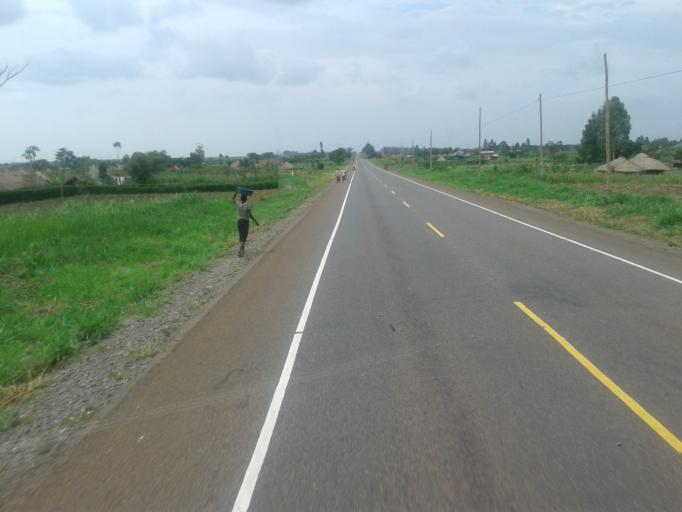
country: UG
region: Western Region
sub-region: Kiryandongo District
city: Kiryandongo
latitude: 2.0089
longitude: 32.1765
